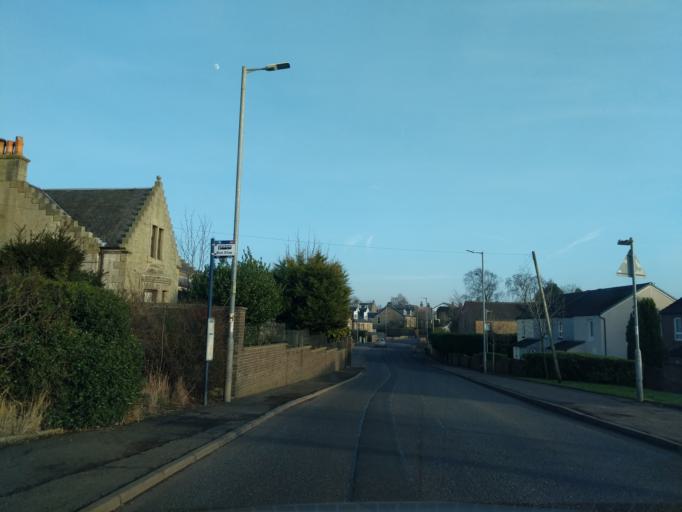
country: GB
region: Scotland
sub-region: South Lanarkshire
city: Carluke
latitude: 55.7372
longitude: -3.8504
